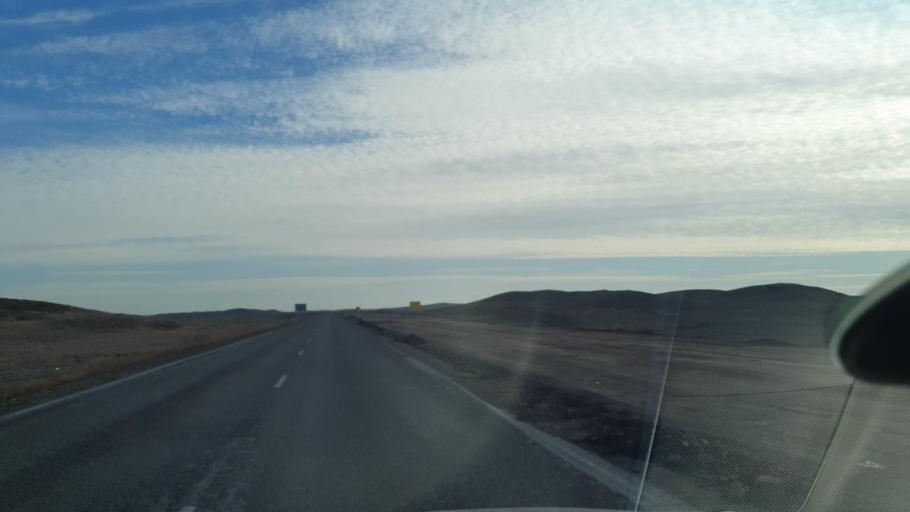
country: KZ
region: Zhambyl
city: Mynaral
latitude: 45.5253
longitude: 73.4845
